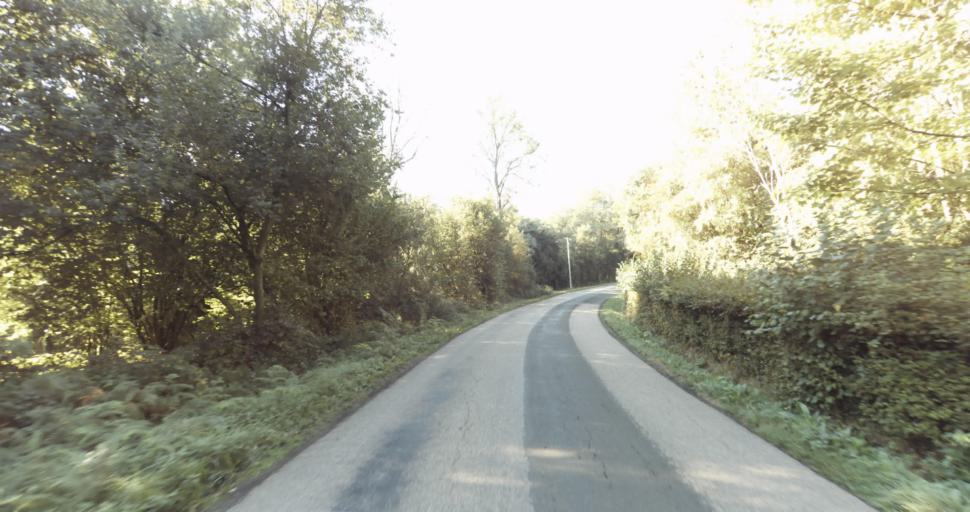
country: FR
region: Lower Normandy
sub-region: Departement de l'Orne
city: Vimoutiers
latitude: 48.9194
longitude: 0.2488
